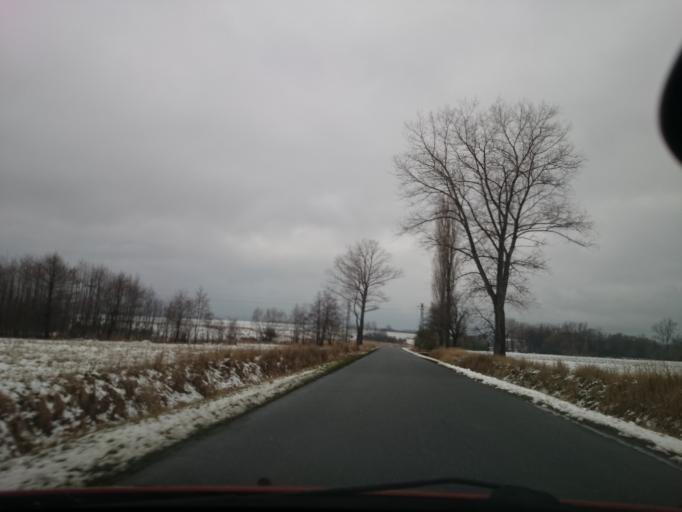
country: PL
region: Lower Silesian Voivodeship
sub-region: Powiat klodzki
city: Klodzko
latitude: 50.3845
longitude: 16.6569
